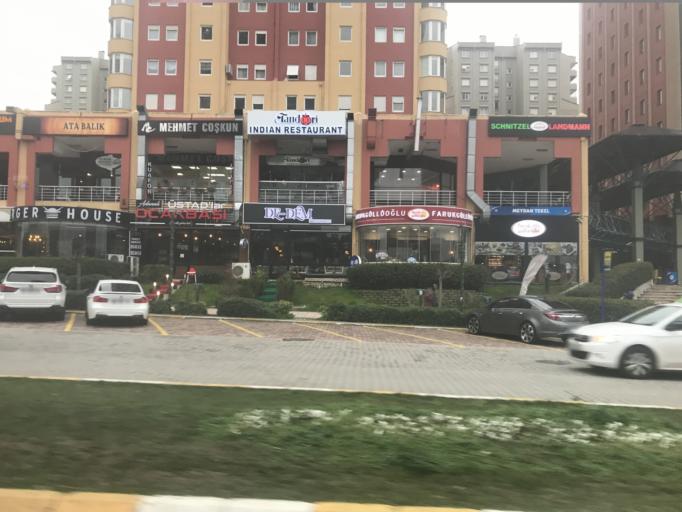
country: TR
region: Istanbul
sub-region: Atasehir
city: Atasehir
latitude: 40.9926
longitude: 29.1191
